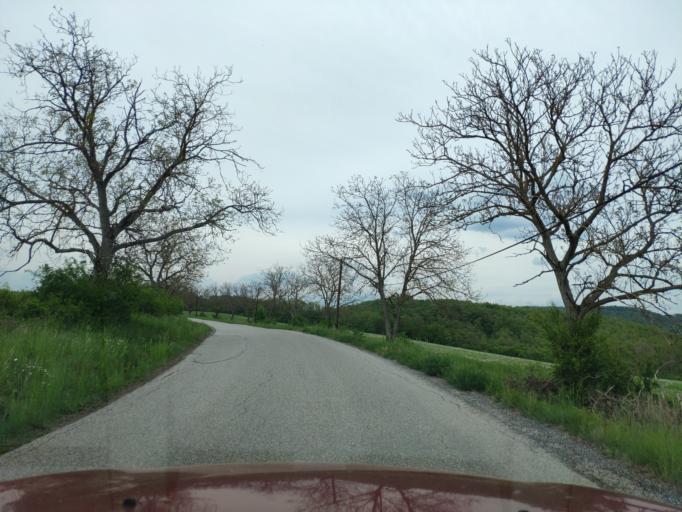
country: SK
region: Banskobystricky
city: Rimavska Sobota
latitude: 48.4899
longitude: 20.0965
